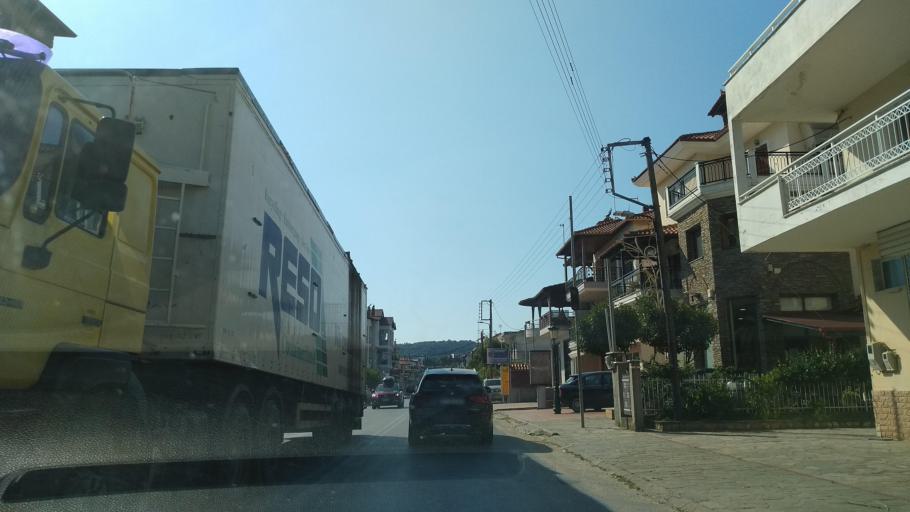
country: GR
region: Central Macedonia
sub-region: Nomos Chalkidikis
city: Ierissos
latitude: 40.4002
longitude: 23.8712
